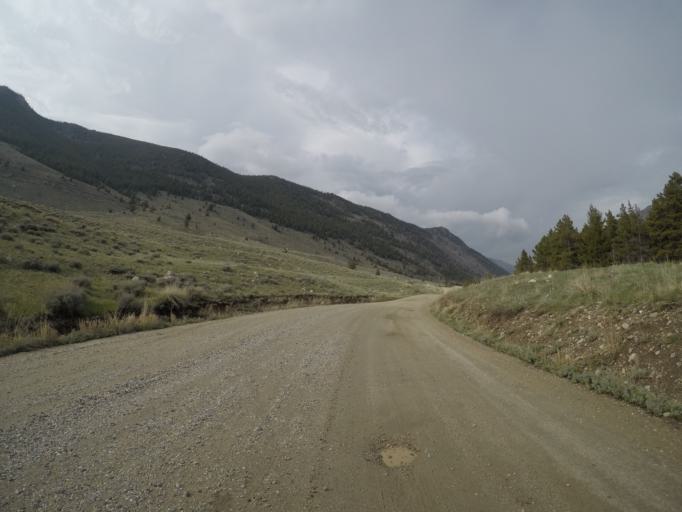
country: US
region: Montana
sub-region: Carbon County
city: Red Lodge
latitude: 45.0567
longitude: -109.4161
